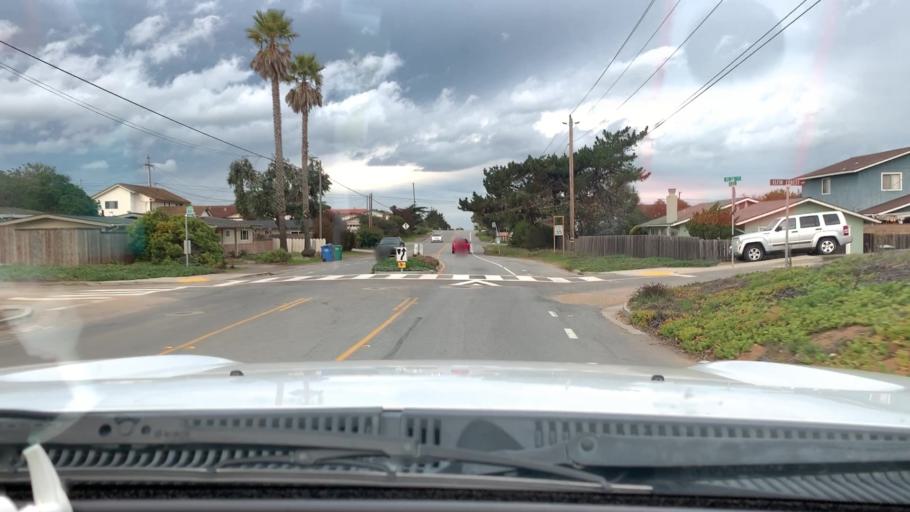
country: US
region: California
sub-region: San Luis Obispo County
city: Los Osos
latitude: 35.3300
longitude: -120.8264
